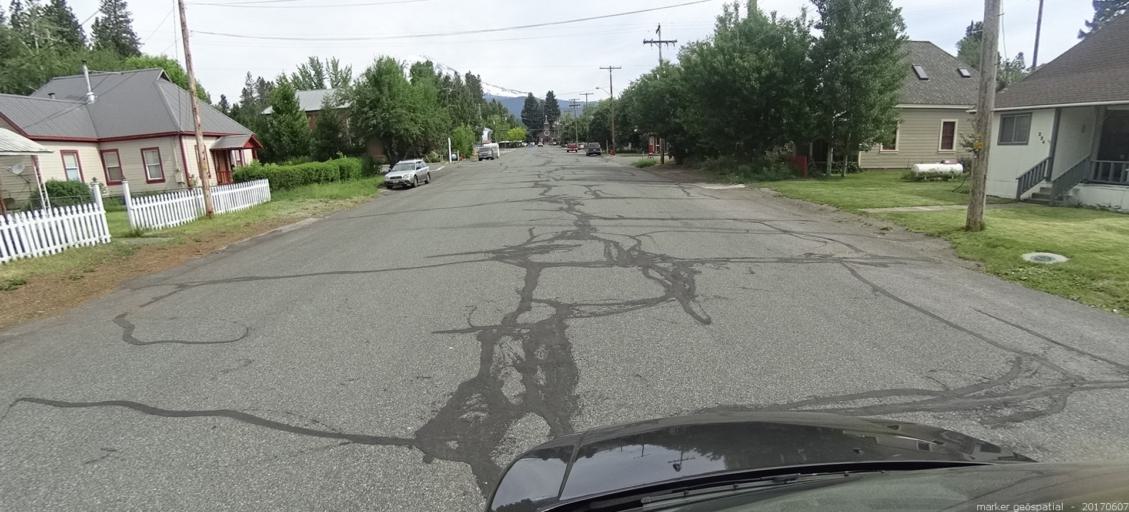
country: US
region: California
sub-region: Siskiyou County
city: McCloud
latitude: 41.2524
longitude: -122.1389
